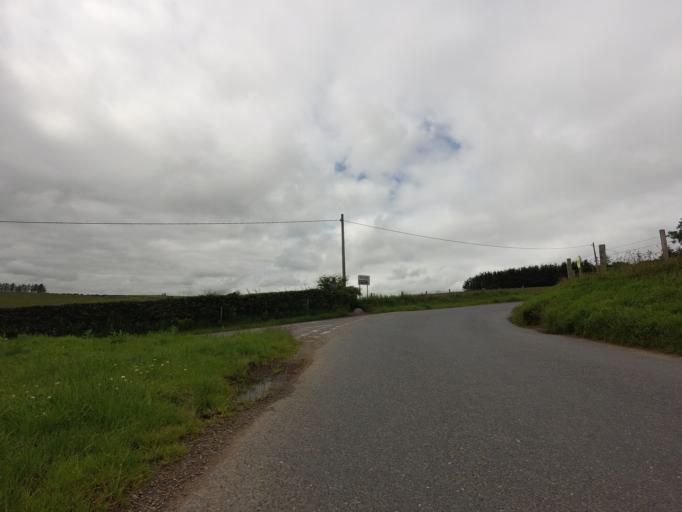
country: GB
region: Scotland
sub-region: Aberdeenshire
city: Rosehearty
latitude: 57.5384
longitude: -2.1891
